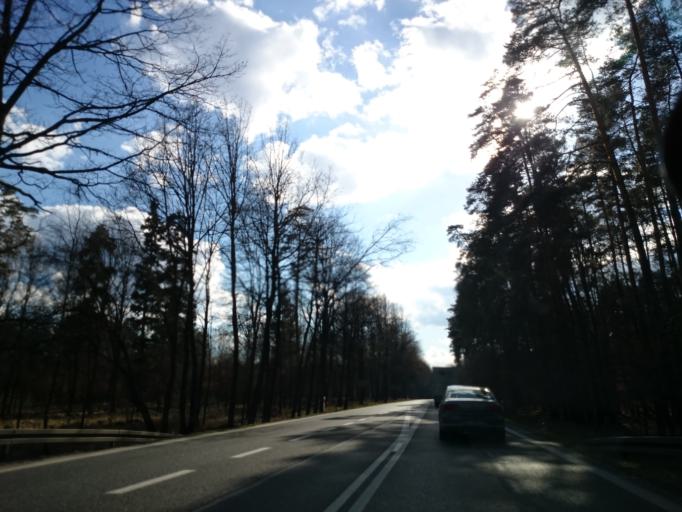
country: PL
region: Opole Voivodeship
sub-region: Powiat opolski
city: Dabrowa
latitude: 50.6793
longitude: 17.7164
